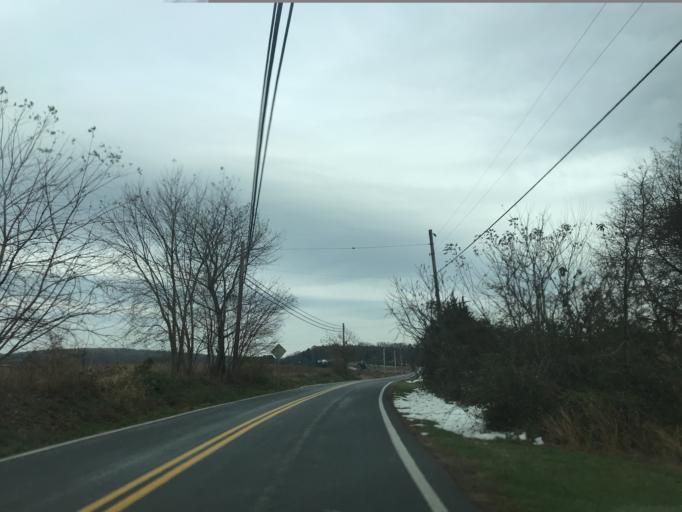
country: US
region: Pennsylvania
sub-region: York County
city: Susquehanna Trails
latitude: 39.6914
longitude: -76.3886
